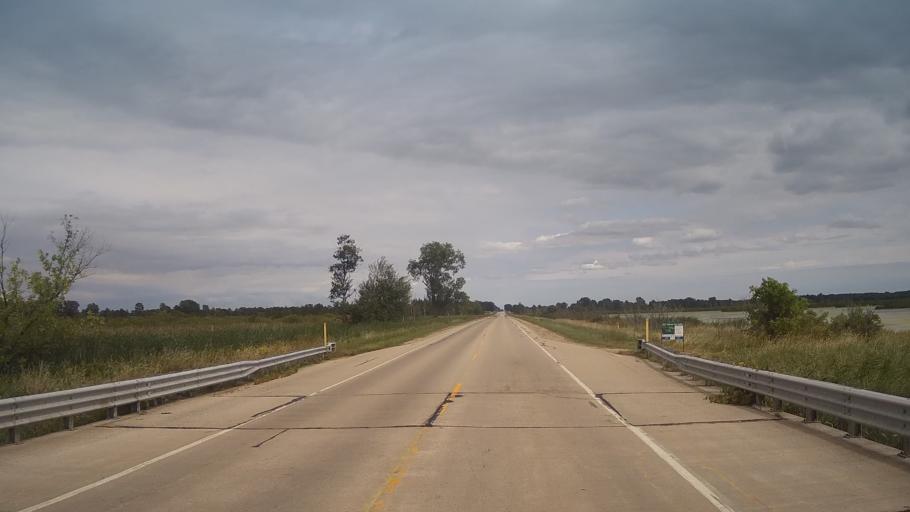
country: US
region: Wisconsin
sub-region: Green Lake County
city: Berlin
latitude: 44.0487
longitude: -88.9616
